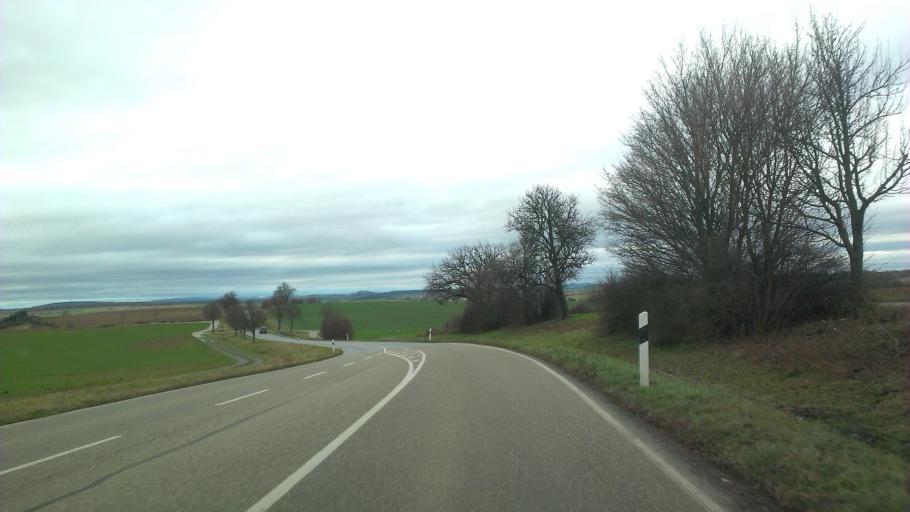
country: DE
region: Baden-Wuerttemberg
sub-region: Regierungsbezirk Stuttgart
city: Eppingen
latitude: 49.1046
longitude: 8.9013
